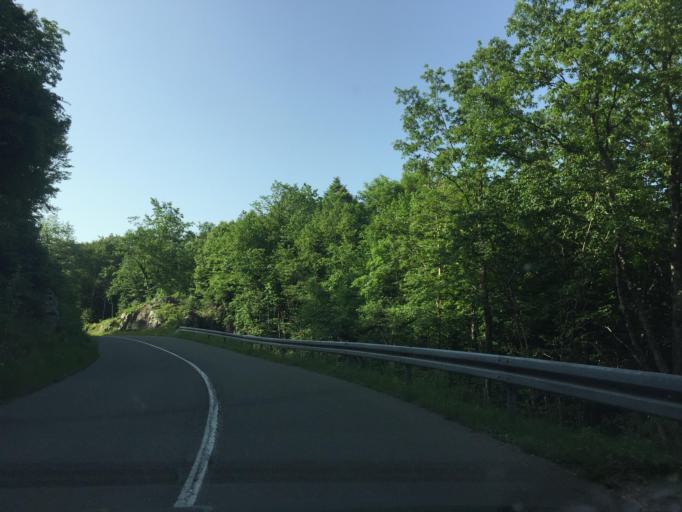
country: HR
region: Primorsko-Goranska
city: Matulji
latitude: 45.4195
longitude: 14.2267
